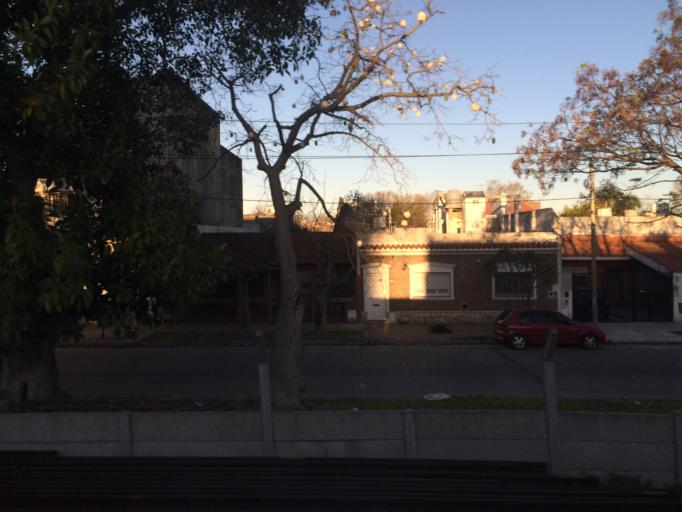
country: AR
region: Buenos Aires
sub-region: Partido de Lanus
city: Lanus
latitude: -34.7136
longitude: -58.3920
